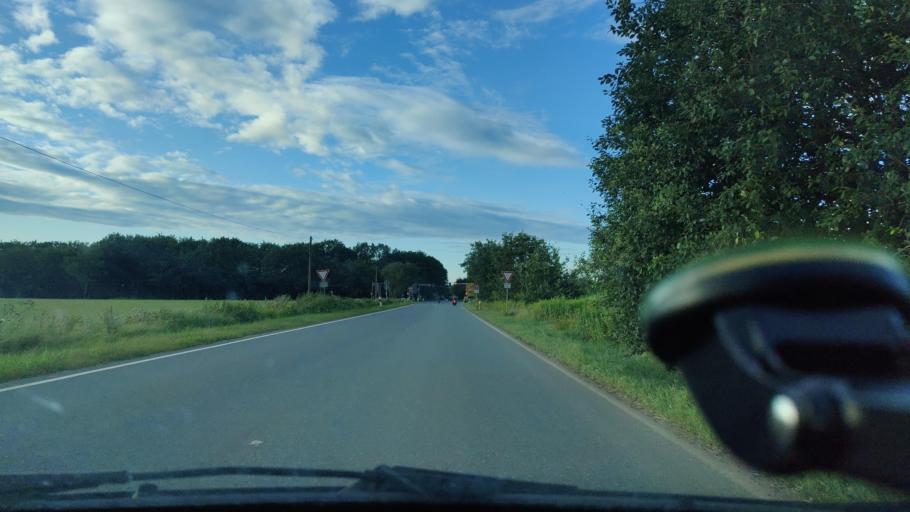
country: DE
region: North Rhine-Westphalia
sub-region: Regierungsbezirk Dusseldorf
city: Schermbeck
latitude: 51.6116
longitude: 6.8916
